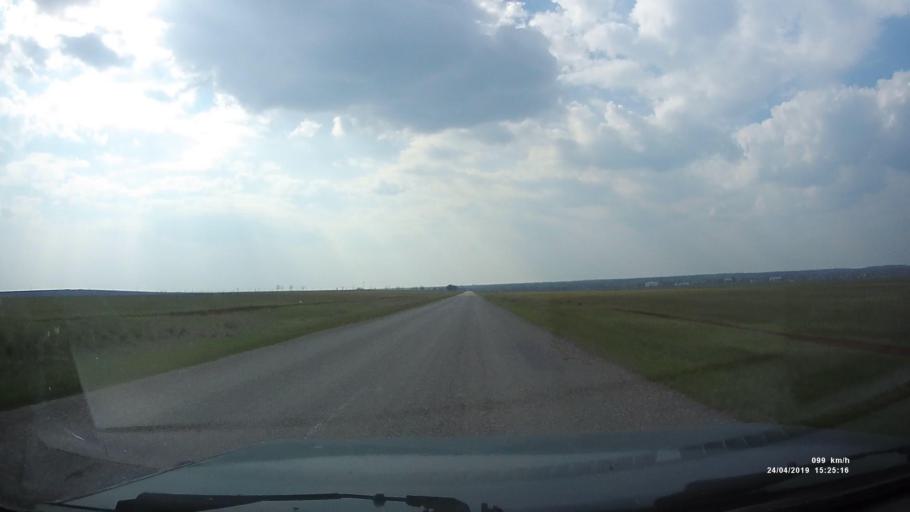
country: RU
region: Rostov
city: Remontnoye
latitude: 46.5516
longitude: 43.0512
